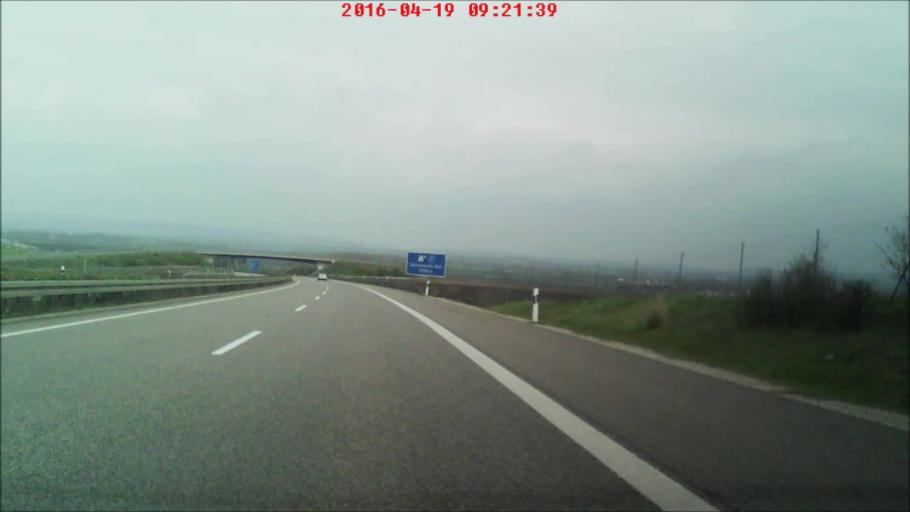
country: DE
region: Thuringia
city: Sprotau
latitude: 51.1416
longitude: 11.1750
